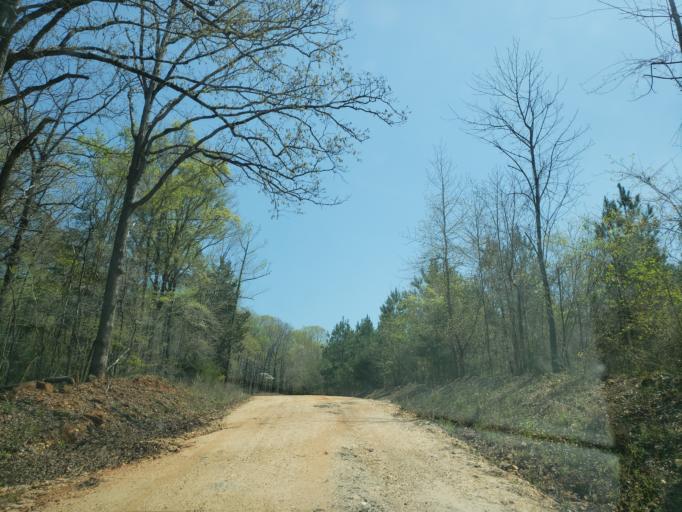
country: US
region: Alabama
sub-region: Tallapoosa County
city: Camp Hill
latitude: 32.6553
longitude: -85.6609
